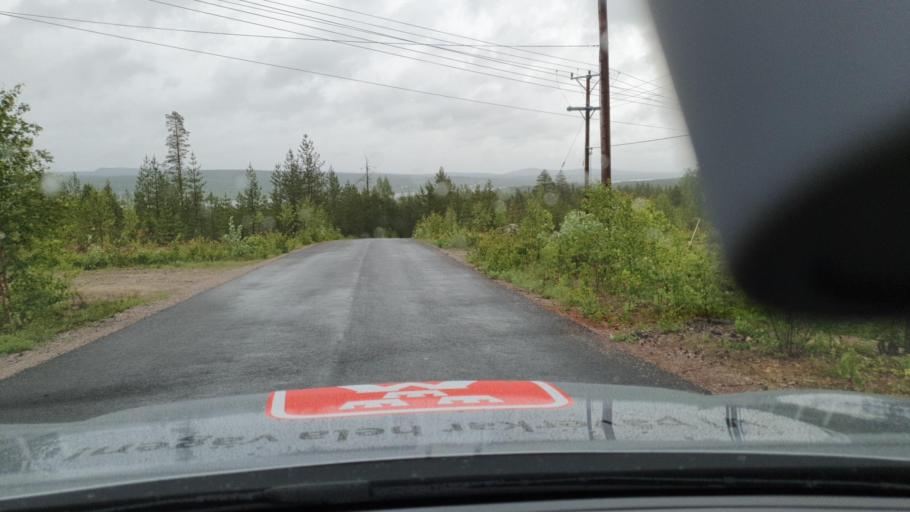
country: FI
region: Lapland
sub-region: Torniolaakso
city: Ylitornio
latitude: 66.3072
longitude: 23.6180
